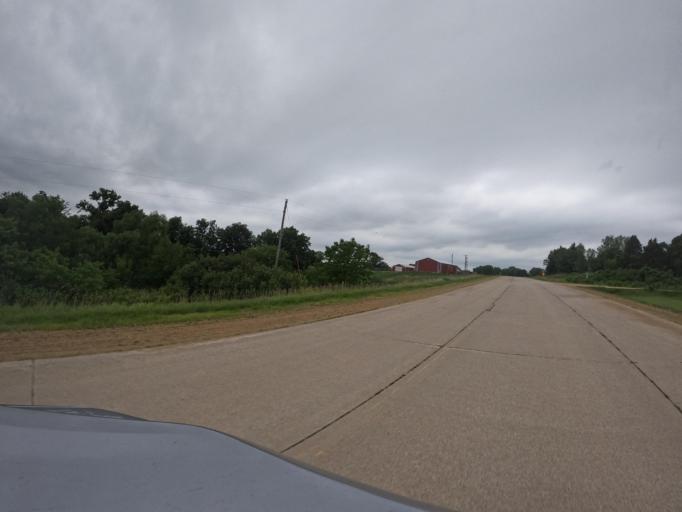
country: US
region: Iowa
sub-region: Jackson County
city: Maquoketa
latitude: 41.9449
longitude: -90.6201
